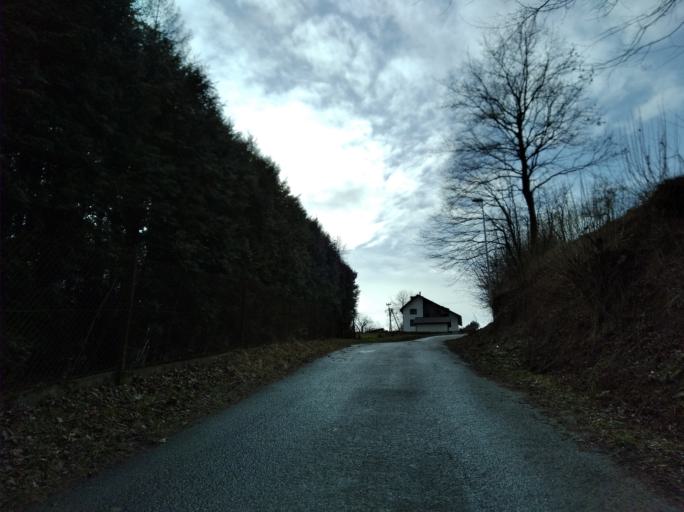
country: PL
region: Subcarpathian Voivodeship
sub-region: Powiat strzyzowski
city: Strzyzow
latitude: 49.8596
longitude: 21.7810
